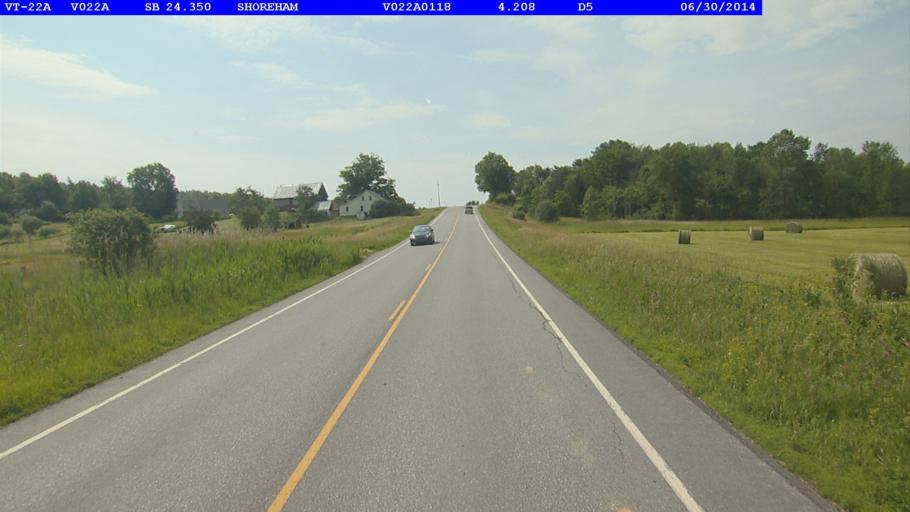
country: US
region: New York
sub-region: Essex County
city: Ticonderoga
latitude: 43.9100
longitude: -73.3100
